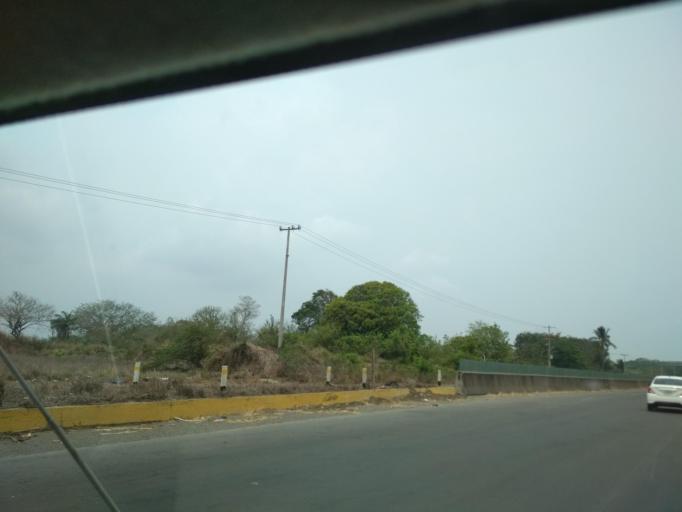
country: MX
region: Veracruz
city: Paso del Toro
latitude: 19.0323
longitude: -96.1470
